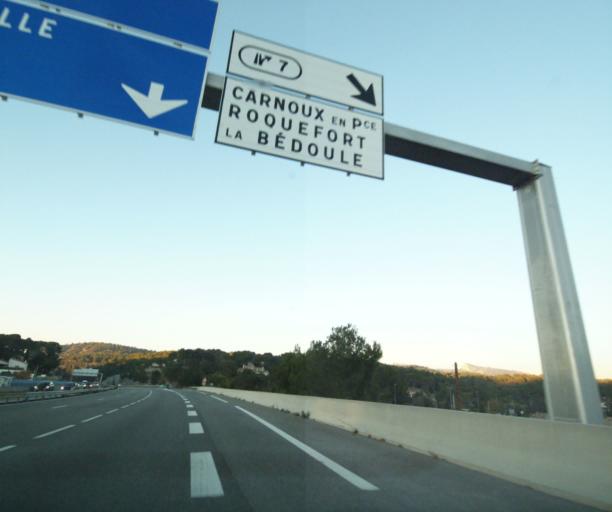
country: FR
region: Provence-Alpes-Cote d'Azur
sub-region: Departement des Bouches-du-Rhone
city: Roquefort-la-Bedoule
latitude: 43.2469
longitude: 5.5965
